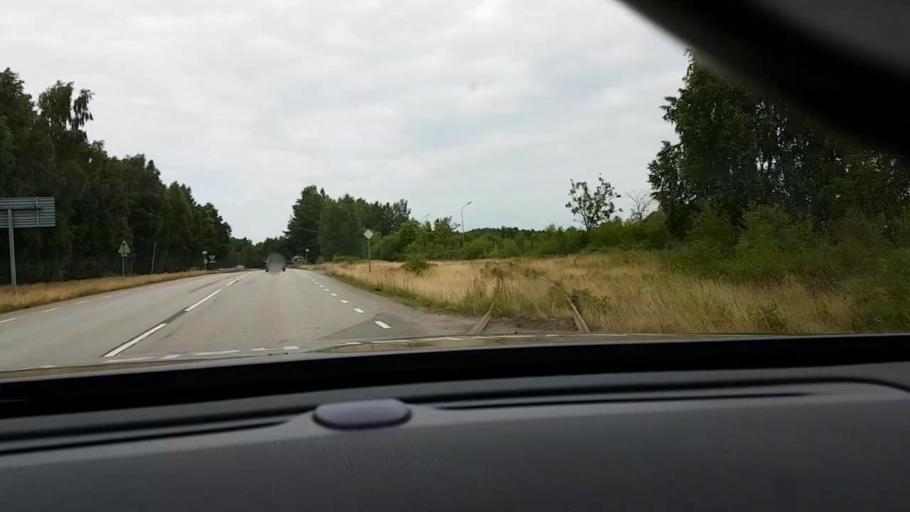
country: SE
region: Skane
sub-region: Hassleholms Kommun
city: Hassleholm
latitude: 56.1600
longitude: 13.8022
